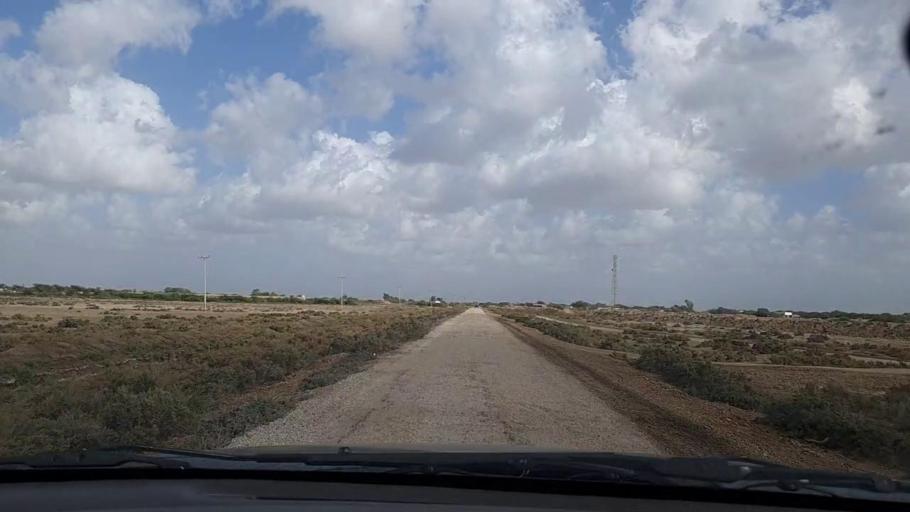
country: PK
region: Sindh
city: Keti Bandar
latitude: 24.1033
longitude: 67.5938
